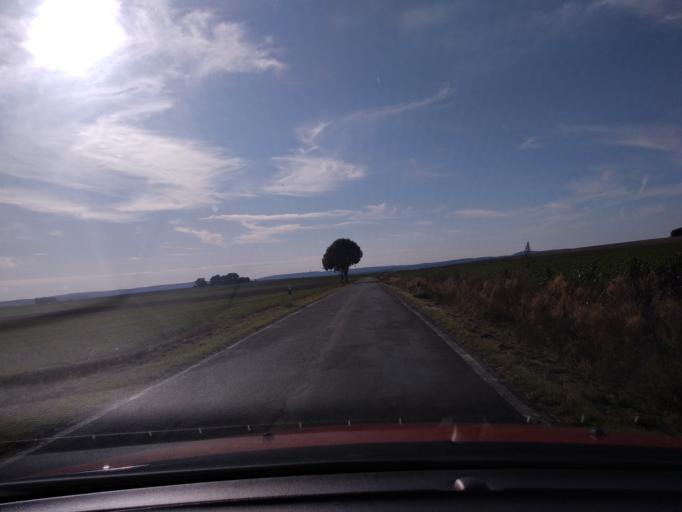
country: DE
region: North Rhine-Westphalia
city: Brakel
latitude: 51.6516
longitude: 9.1757
